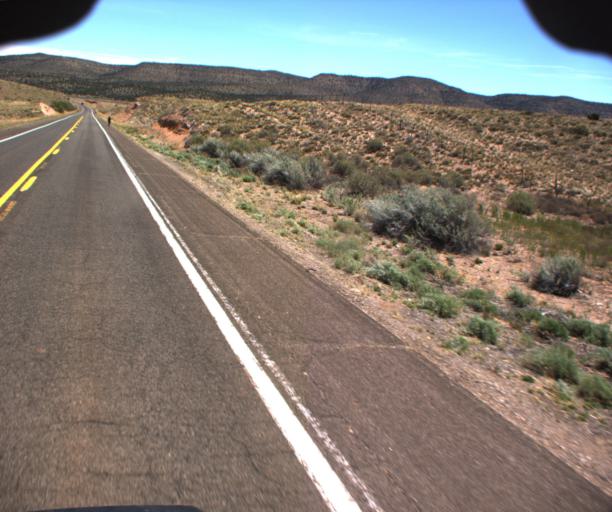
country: US
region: Arizona
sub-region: Mohave County
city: Peach Springs
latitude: 35.5229
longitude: -113.4647
